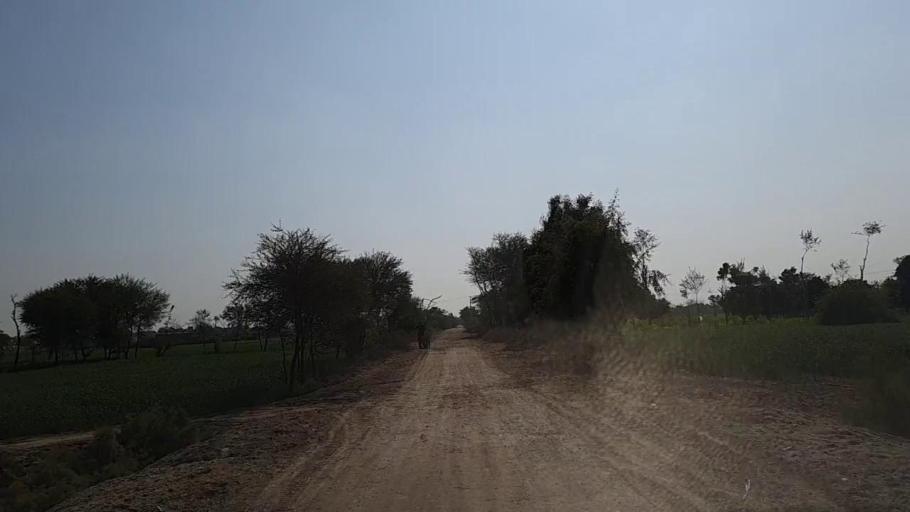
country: PK
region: Sindh
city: Jam Sahib
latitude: 26.2665
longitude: 68.5287
